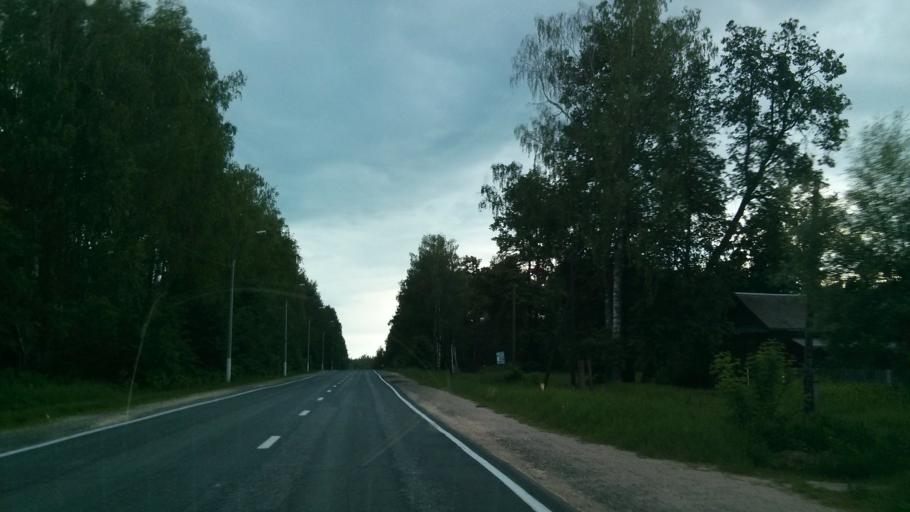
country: RU
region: Nizjnij Novgorod
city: Vacha
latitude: 55.7505
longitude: 42.5080
